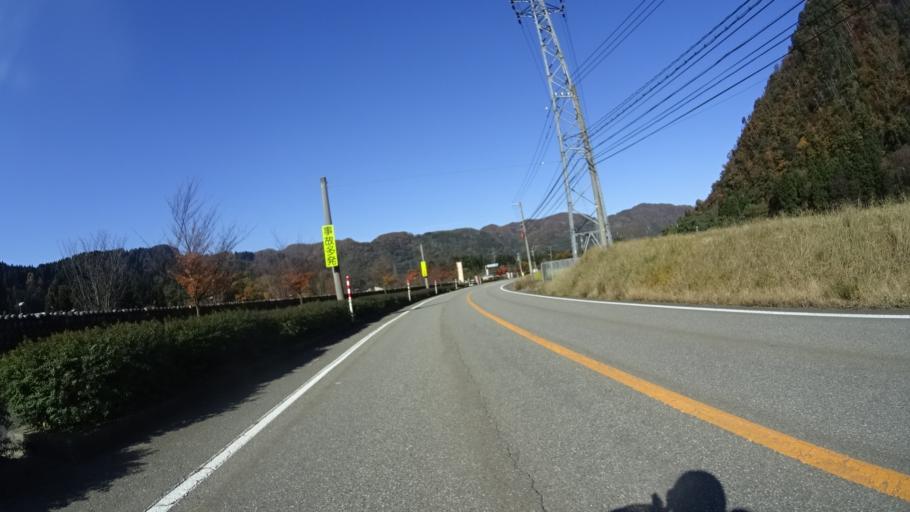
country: JP
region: Ishikawa
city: Tsurugi-asahimachi
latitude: 36.3644
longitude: 136.6135
